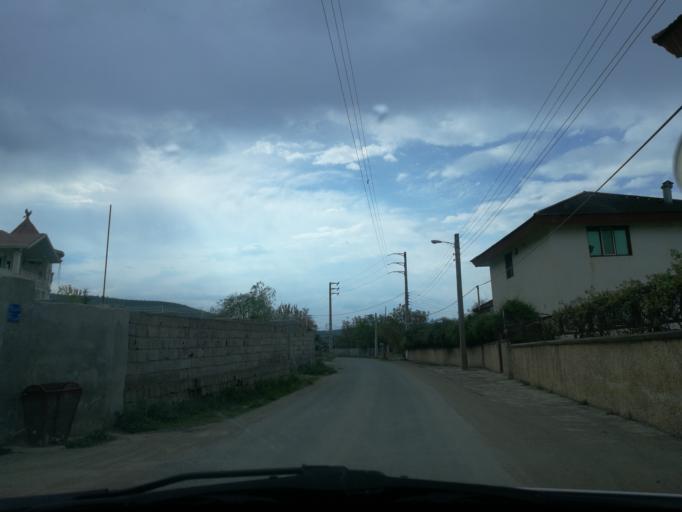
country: IR
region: Mazandaran
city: `Abbasabad
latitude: 36.5335
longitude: 51.2241
